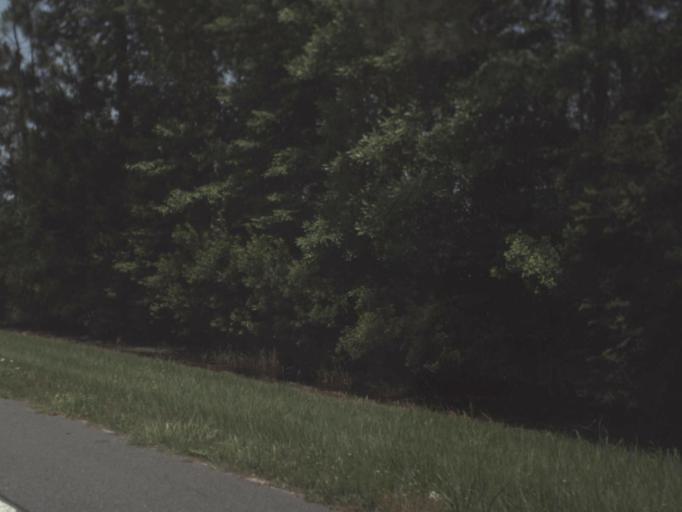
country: US
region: Florida
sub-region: Duval County
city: Baldwin
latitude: 30.2063
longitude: -81.9777
